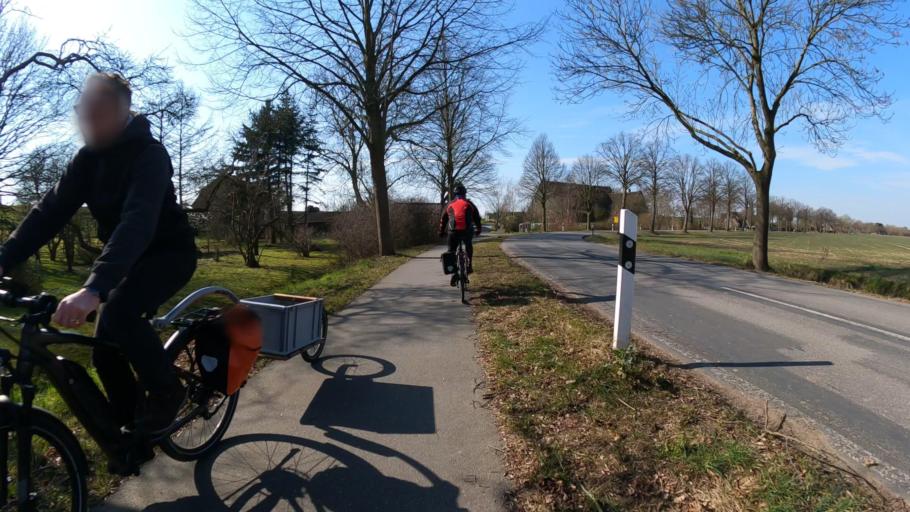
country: DE
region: Schleswig-Holstein
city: Neuendeich
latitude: 53.6741
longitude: 9.5860
